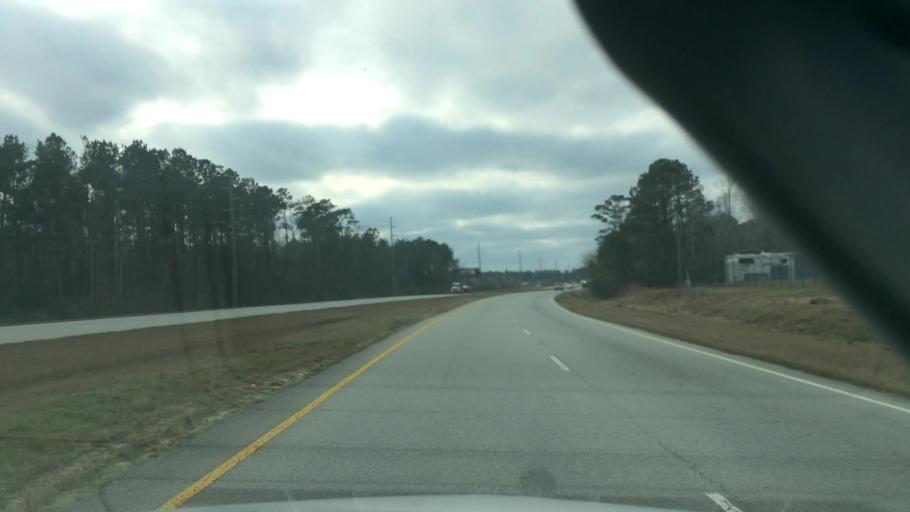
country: US
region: North Carolina
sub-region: Brunswick County
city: Shallotte
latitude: 33.9590
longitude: -78.4217
